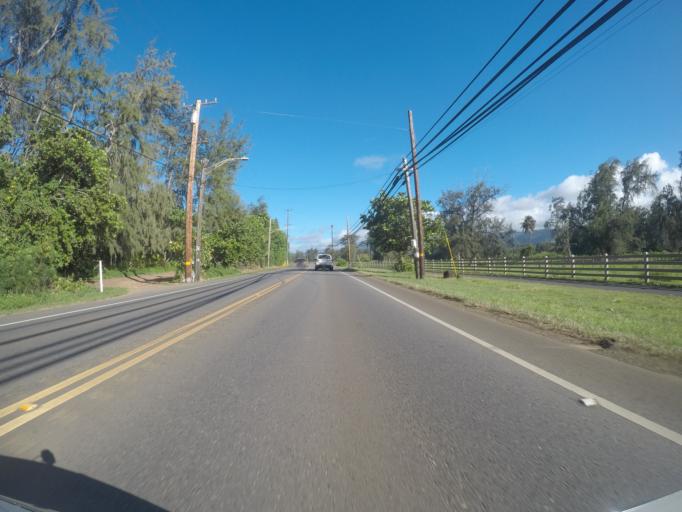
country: US
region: Hawaii
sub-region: Honolulu County
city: Kahuku
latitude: 21.6680
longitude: -157.9383
